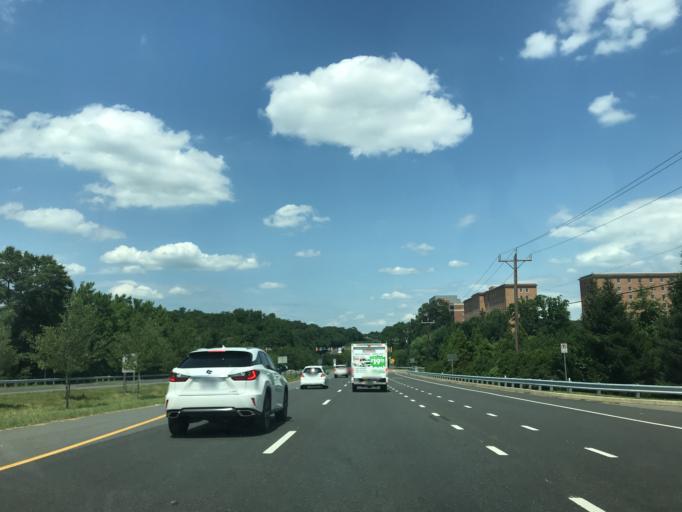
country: US
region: Maryland
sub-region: Prince George's County
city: College Park
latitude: 38.9911
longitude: -76.9524
